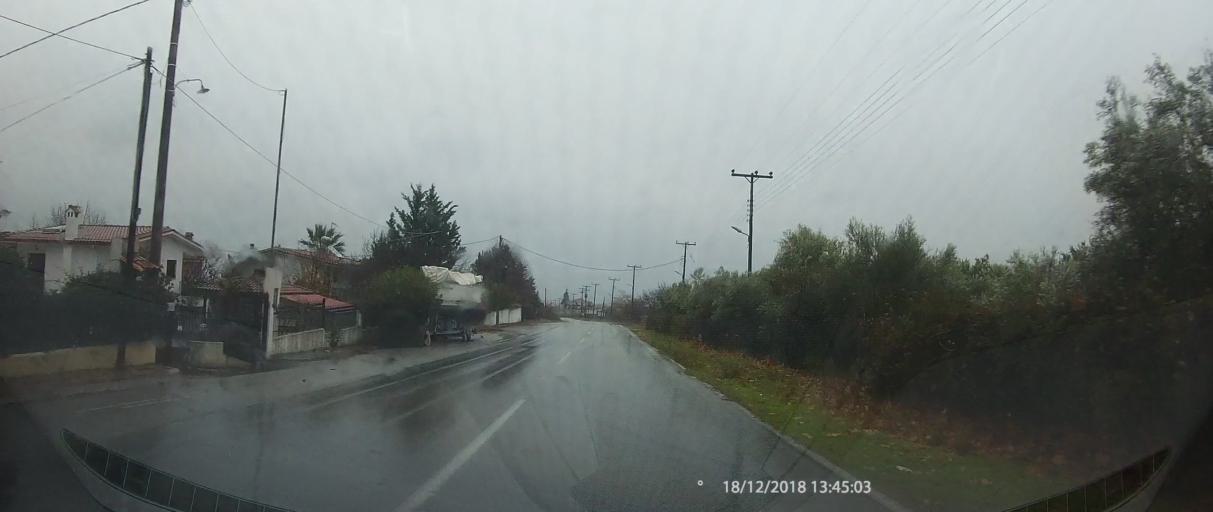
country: GR
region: Central Macedonia
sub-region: Nomos Pierias
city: Litochoro
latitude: 40.0991
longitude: 22.5388
